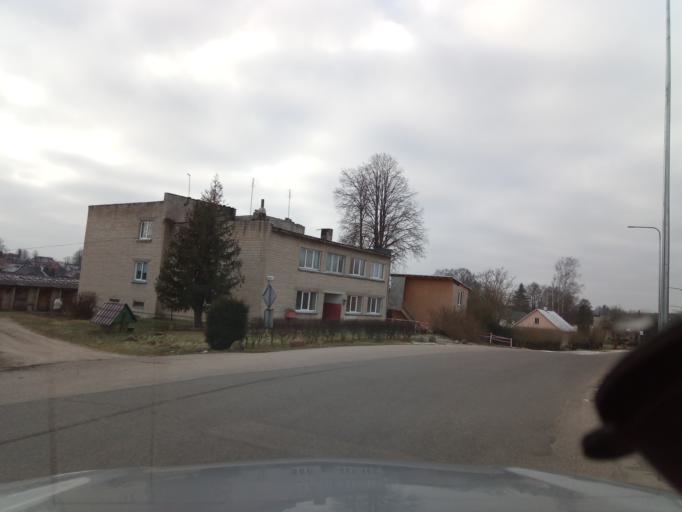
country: LT
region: Alytaus apskritis
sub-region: Alytaus rajonas
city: Daugai
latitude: 54.3657
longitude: 24.3464
